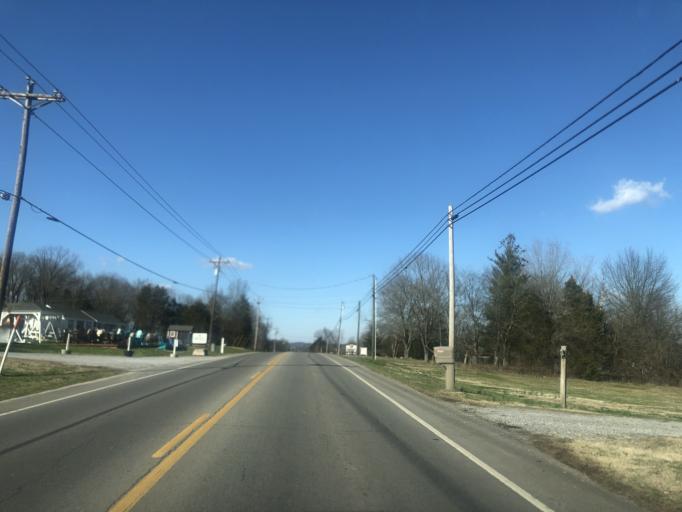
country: US
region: Tennessee
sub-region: Williamson County
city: Nolensville
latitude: 35.9455
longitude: -86.6654
